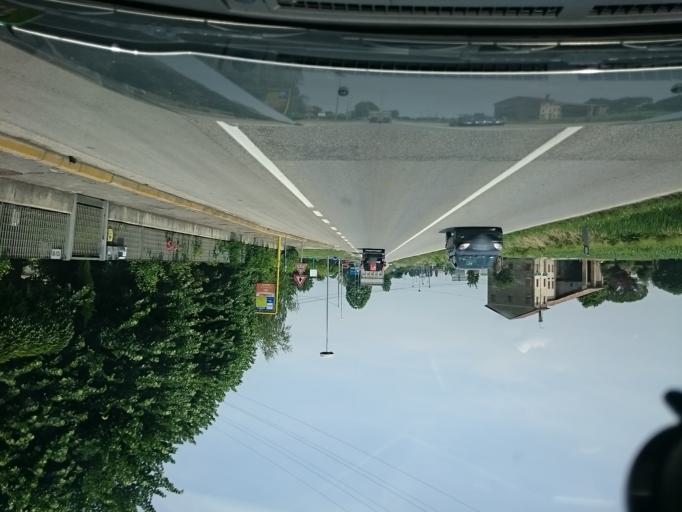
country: IT
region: Veneto
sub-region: Provincia di Padova
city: Legnaro
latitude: 45.3559
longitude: 11.9484
